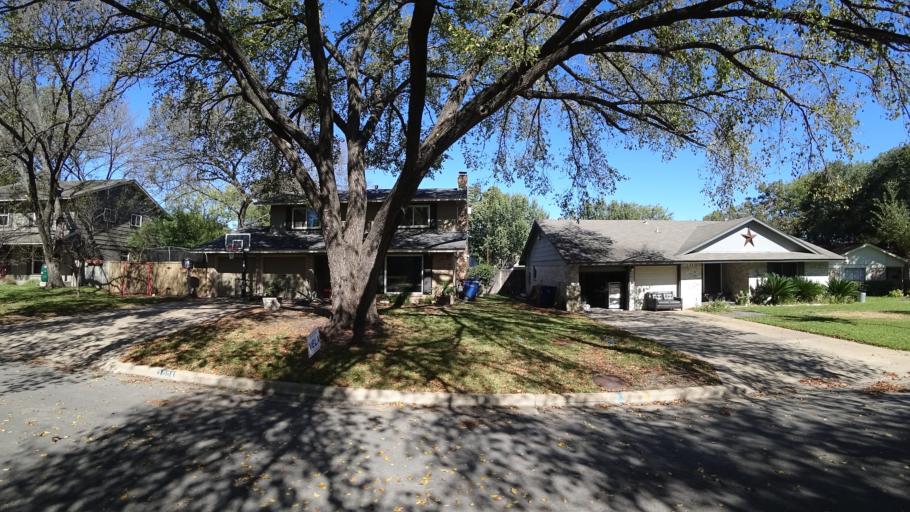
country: US
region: Texas
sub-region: Travis County
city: Austin
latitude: 30.3051
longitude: -97.6899
